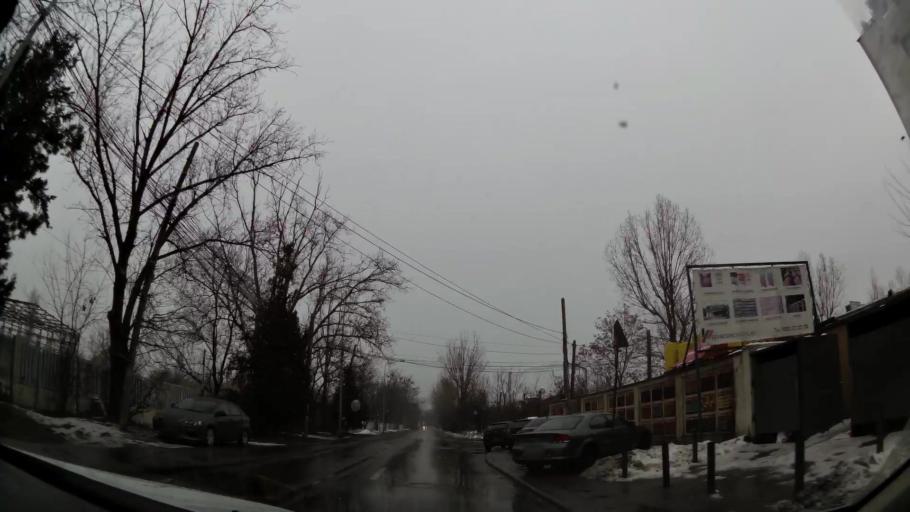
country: RO
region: Ilfov
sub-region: Comuna Otopeni
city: Otopeni
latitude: 44.4888
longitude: 26.0653
